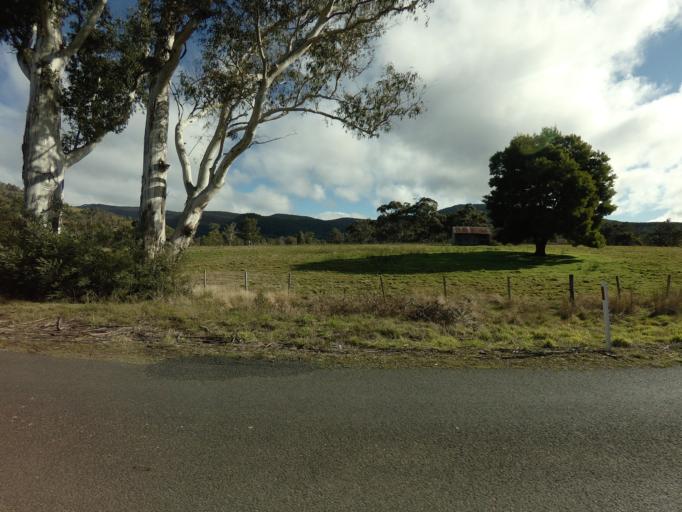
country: AU
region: Tasmania
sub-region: Derwent Valley
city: New Norfolk
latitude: -42.6031
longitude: 146.7061
